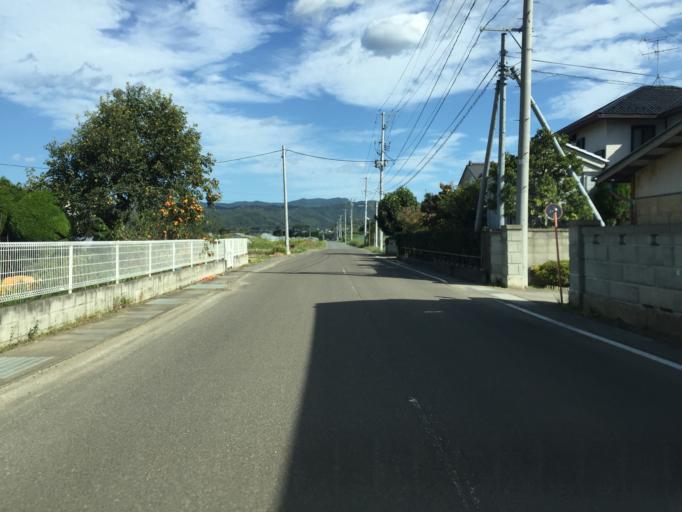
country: JP
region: Fukushima
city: Yanagawamachi-saiwaicho
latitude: 37.8416
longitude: 140.5846
